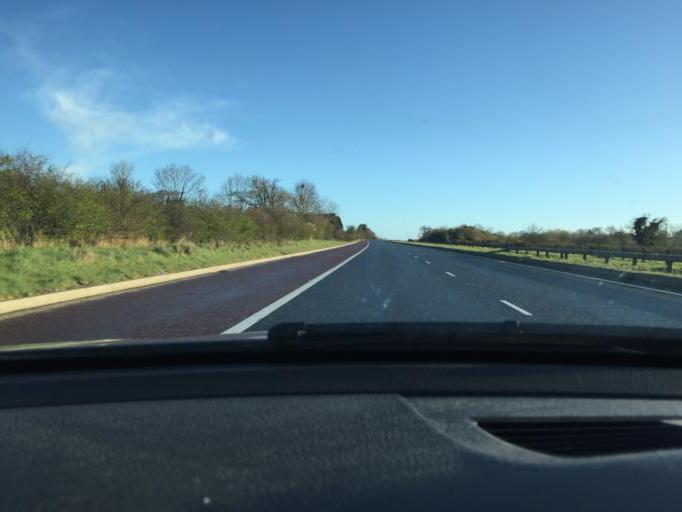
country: GB
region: Northern Ireland
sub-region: Newry and Mourne District
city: Newry
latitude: 54.2554
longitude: -6.3189
